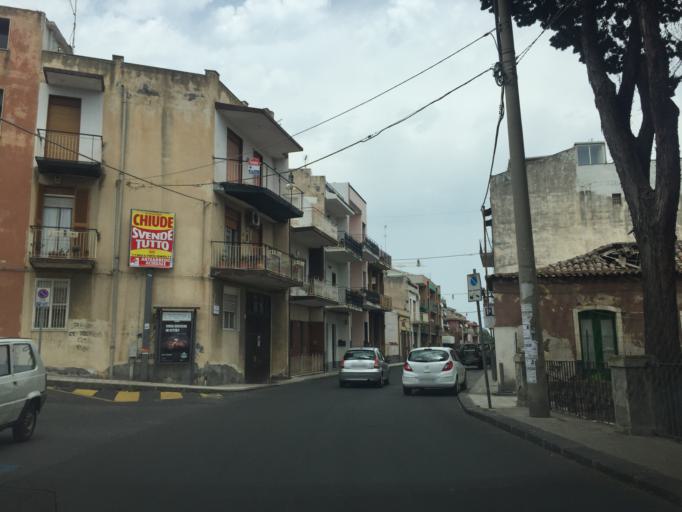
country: IT
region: Sicily
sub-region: Catania
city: Aci Castello
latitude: 37.5575
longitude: 15.1484
